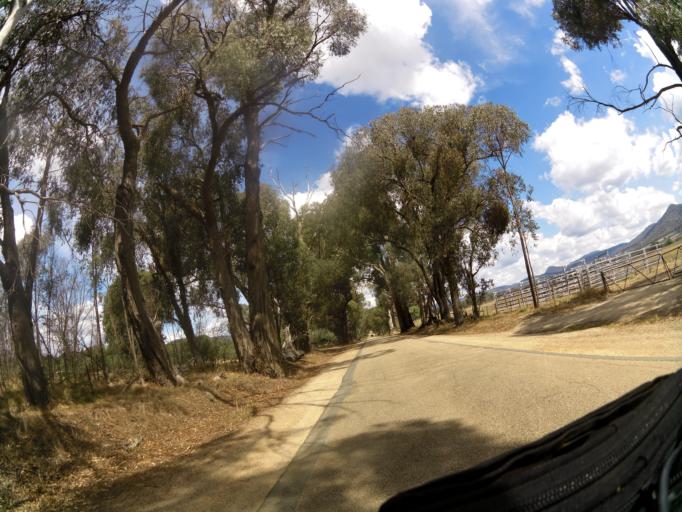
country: AU
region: Victoria
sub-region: Benalla
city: Benalla
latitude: -36.7702
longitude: 145.9751
